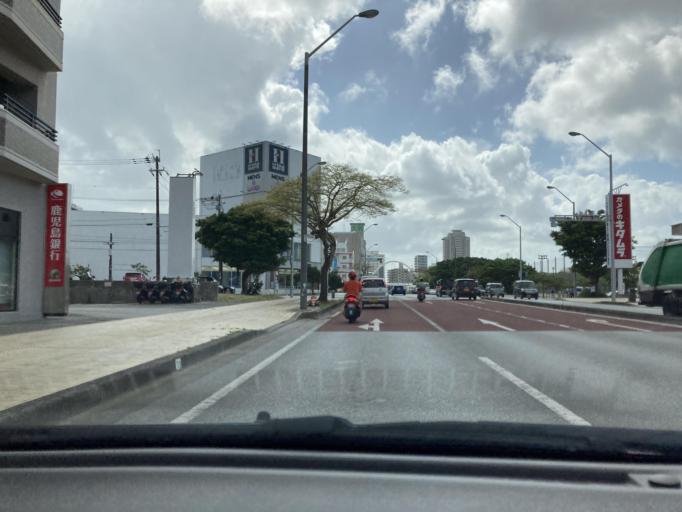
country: JP
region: Okinawa
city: Naha-shi
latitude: 26.2293
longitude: 127.6982
